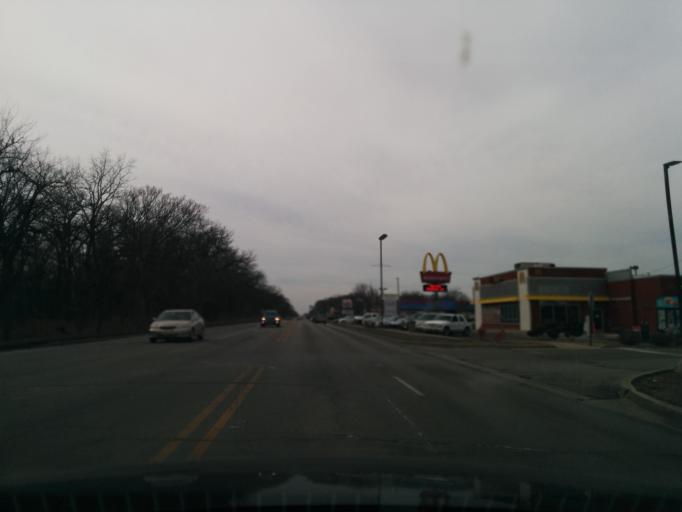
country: US
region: Illinois
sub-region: Cook County
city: Westchester
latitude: 41.8337
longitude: -87.8969
